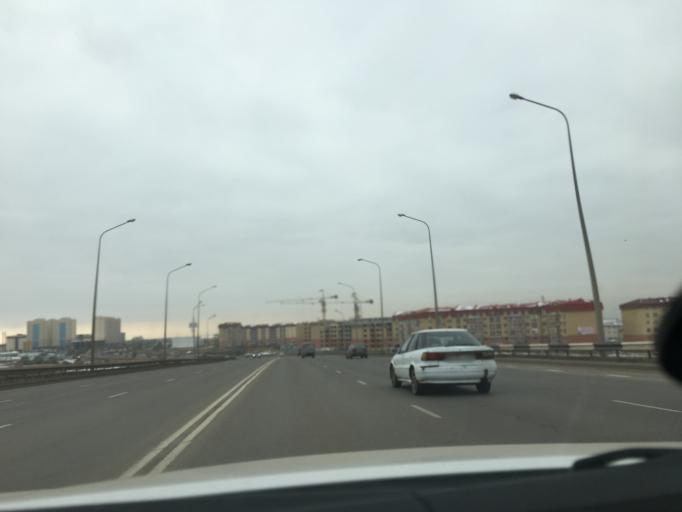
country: KZ
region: Astana Qalasy
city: Astana
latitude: 51.1517
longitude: 71.5322
